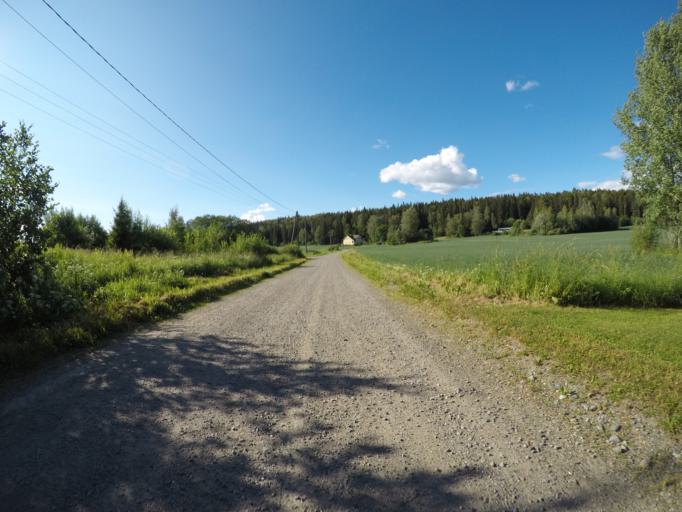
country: FI
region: Haeme
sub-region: Haemeenlinna
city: Haemeenlinna
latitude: 61.0206
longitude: 24.5001
